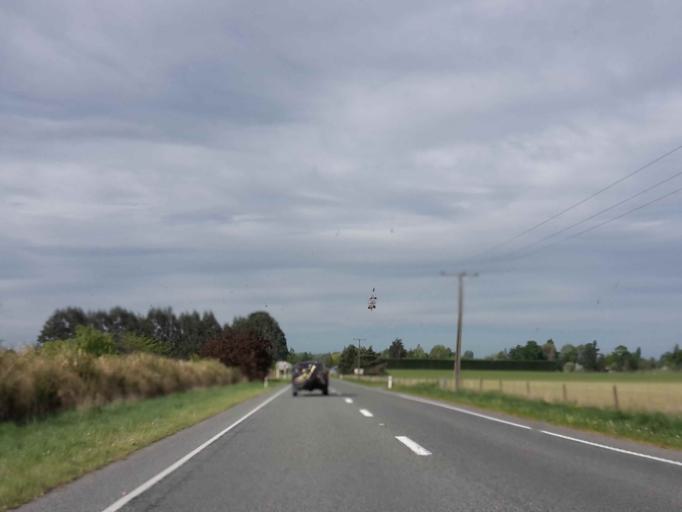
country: NZ
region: Canterbury
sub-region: Timaru District
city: Pleasant Point
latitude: -44.1105
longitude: 171.2288
